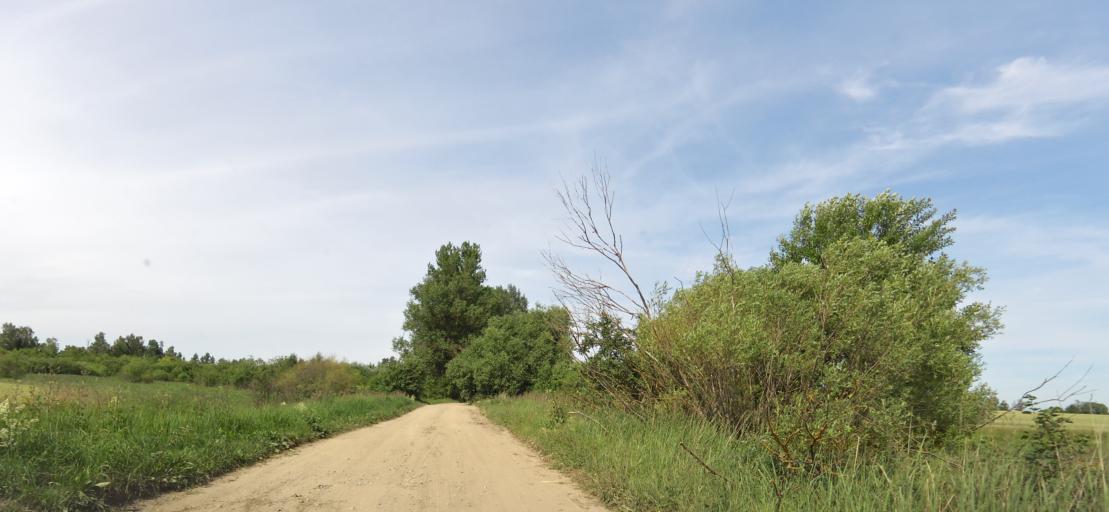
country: LT
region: Panevezys
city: Pasvalys
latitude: 55.9138
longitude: 24.2925
